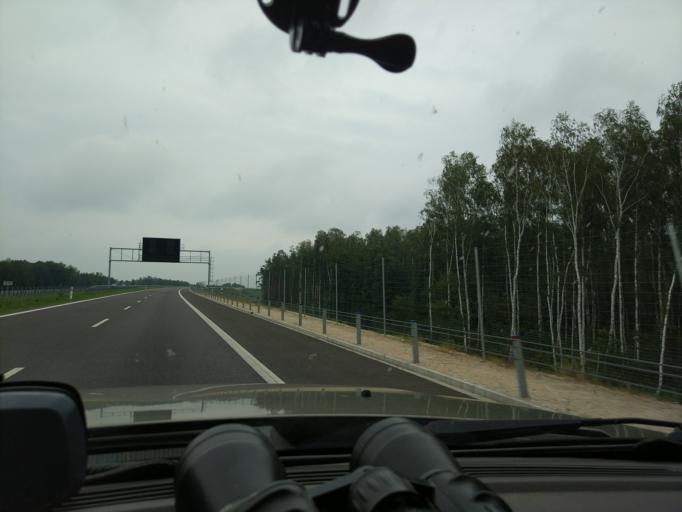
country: PL
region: Podlasie
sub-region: Powiat zambrowski
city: Szumowo
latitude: 52.9389
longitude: 22.1456
